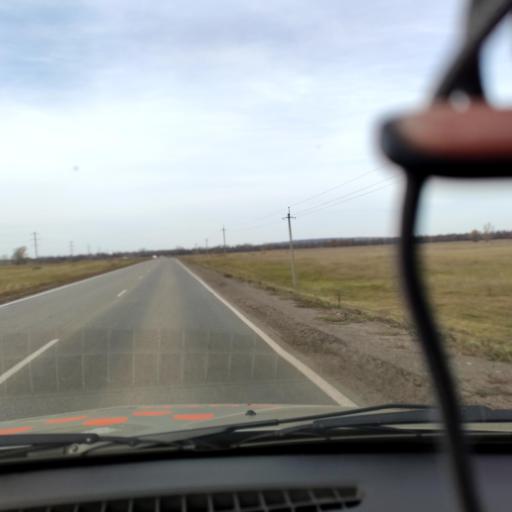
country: RU
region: Bashkortostan
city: Kabakovo
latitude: 54.5571
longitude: 56.0147
